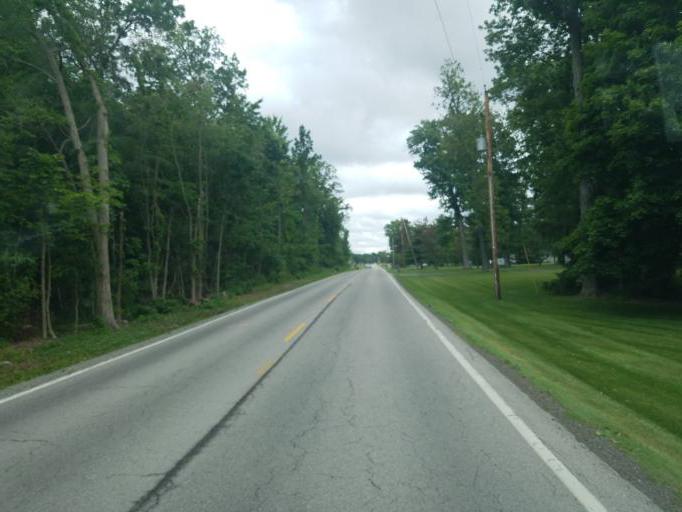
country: US
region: Ohio
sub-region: Crawford County
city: Bucyrus
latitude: 40.7655
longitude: -82.9207
